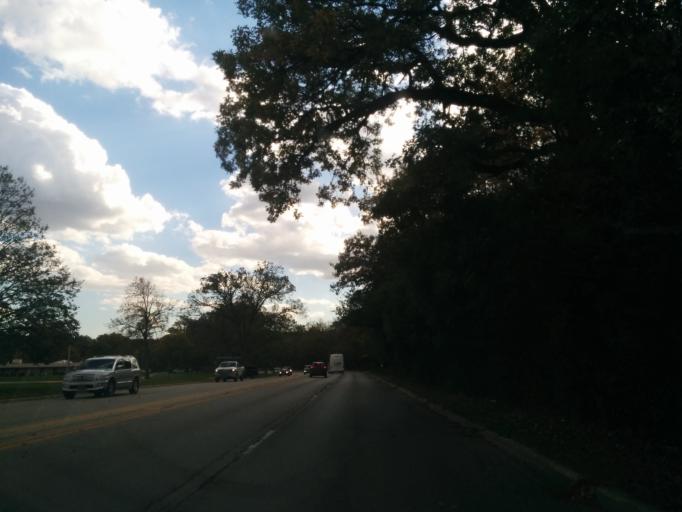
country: US
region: Illinois
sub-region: Cook County
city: Park Ridge
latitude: 41.9988
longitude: -87.8553
